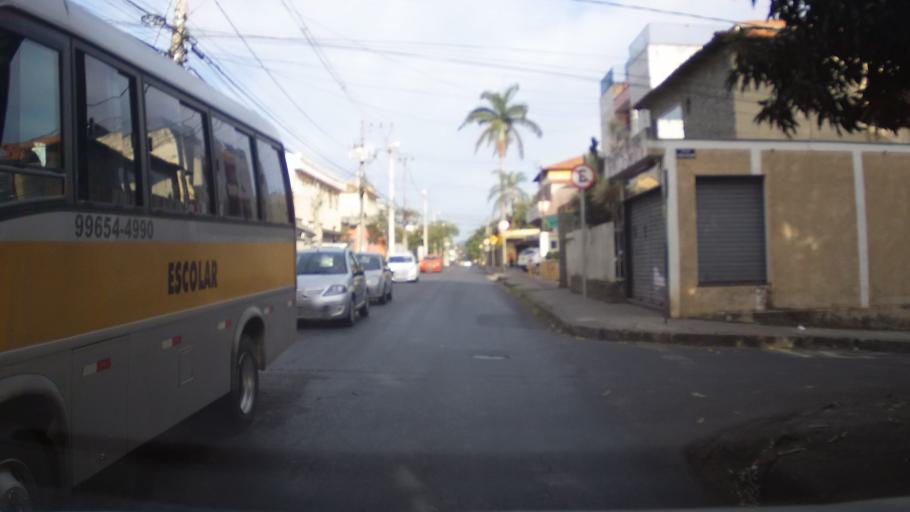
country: BR
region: Minas Gerais
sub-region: Belo Horizonte
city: Belo Horizonte
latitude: -19.8703
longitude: -43.9929
